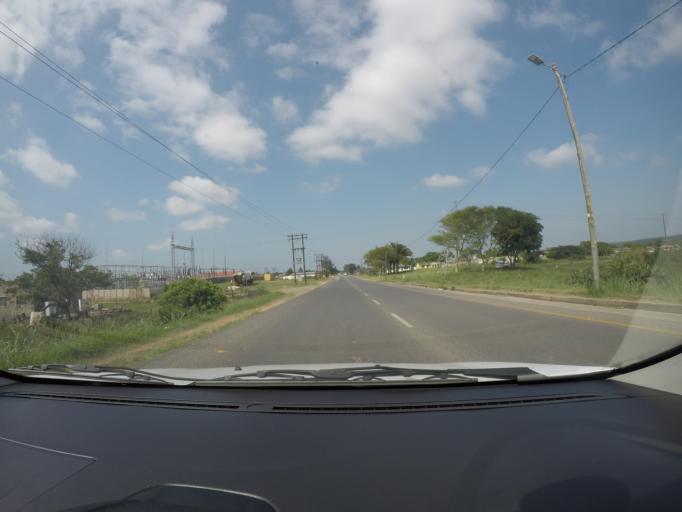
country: ZA
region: KwaZulu-Natal
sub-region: uThungulu District Municipality
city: eSikhawini
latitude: -28.8849
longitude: 31.9011
